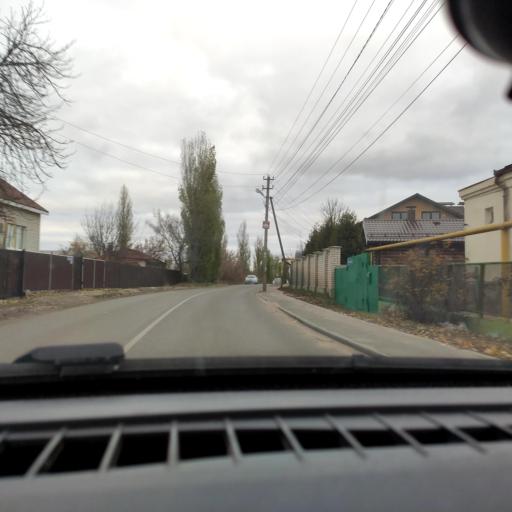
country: RU
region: Voronezj
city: Podgornoye
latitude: 51.7302
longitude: 39.1376
